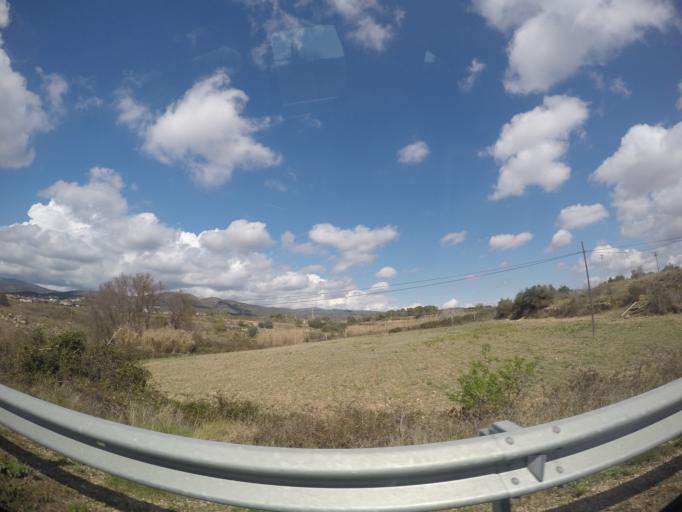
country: ES
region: Catalonia
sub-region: Provincia de Tarragona
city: Santa Oliva
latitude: 41.2829
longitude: 1.5322
